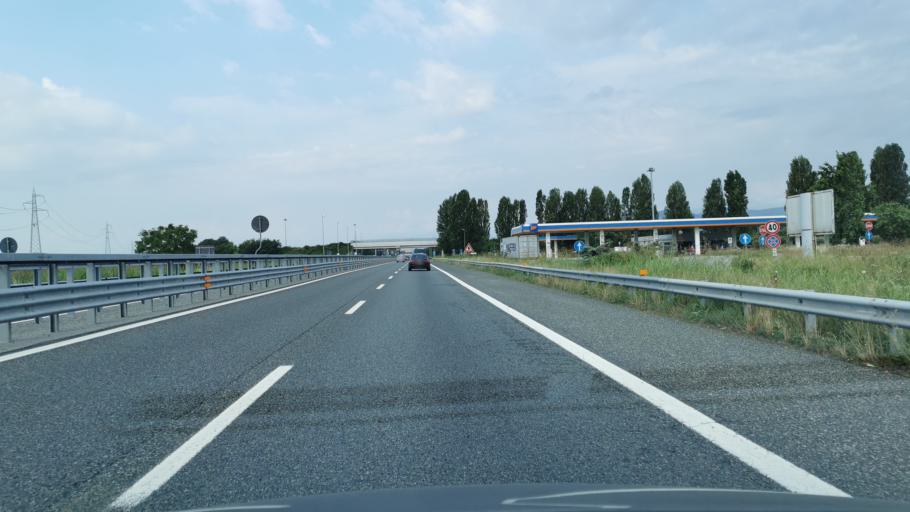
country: IT
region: Piedmont
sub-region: Provincia di Torino
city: Borgo Melano
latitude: 45.0126
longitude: 7.5830
